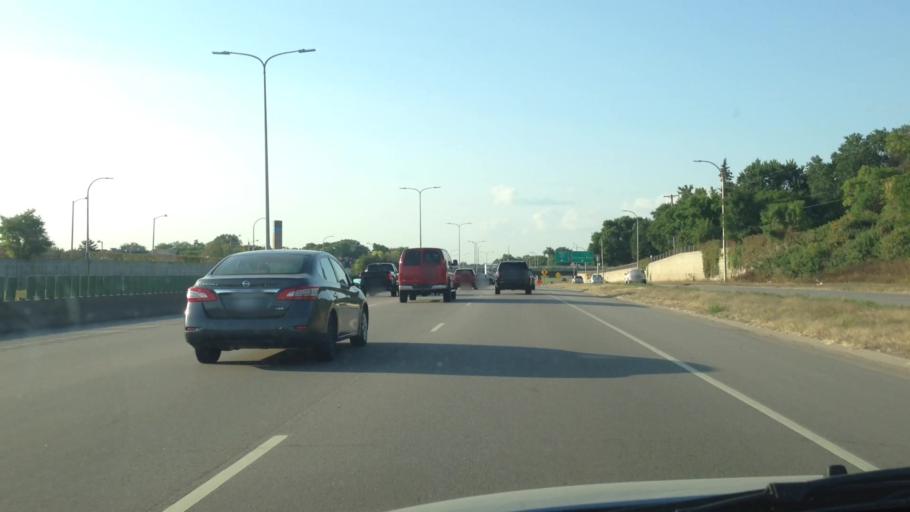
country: US
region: Minnesota
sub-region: Hennepin County
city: Saint Louis Park
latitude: 44.9330
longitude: -93.3476
